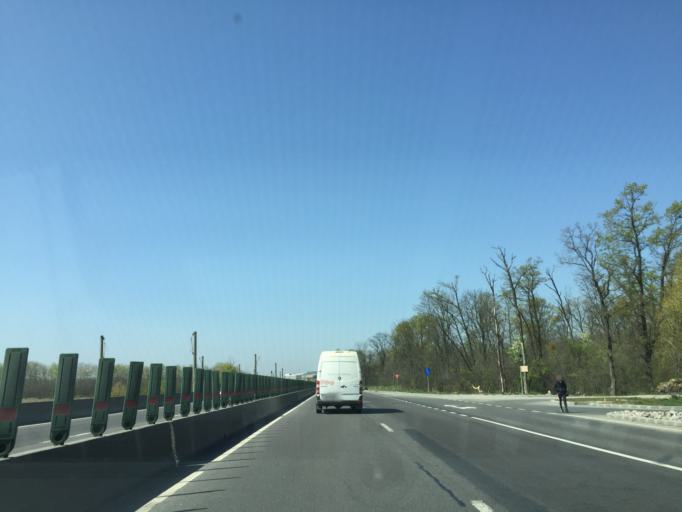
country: RO
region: Ilfov
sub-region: Comuna Otopeni
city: Otopeni
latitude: 44.5395
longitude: 26.1025
